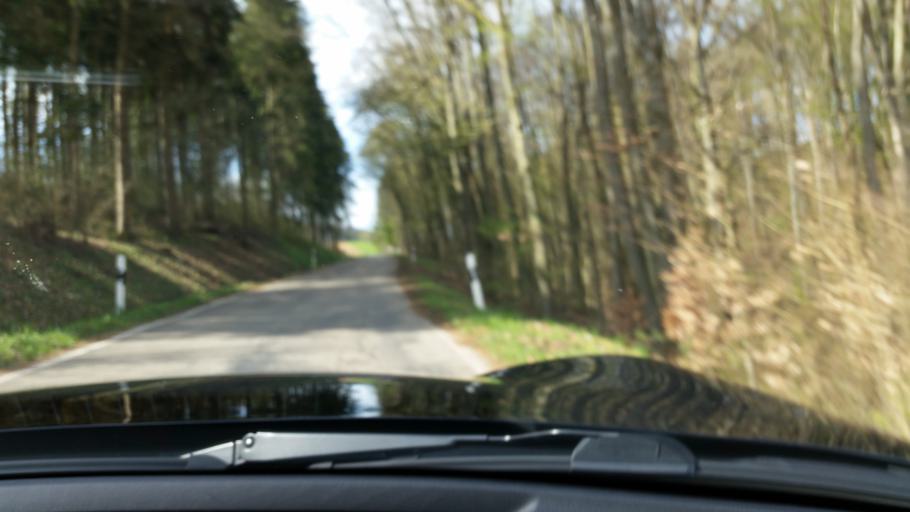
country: DE
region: Baden-Wuerttemberg
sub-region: Regierungsbezirk Stuttgart
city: Jagsthausen
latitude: 49.3606
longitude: 9.4661
